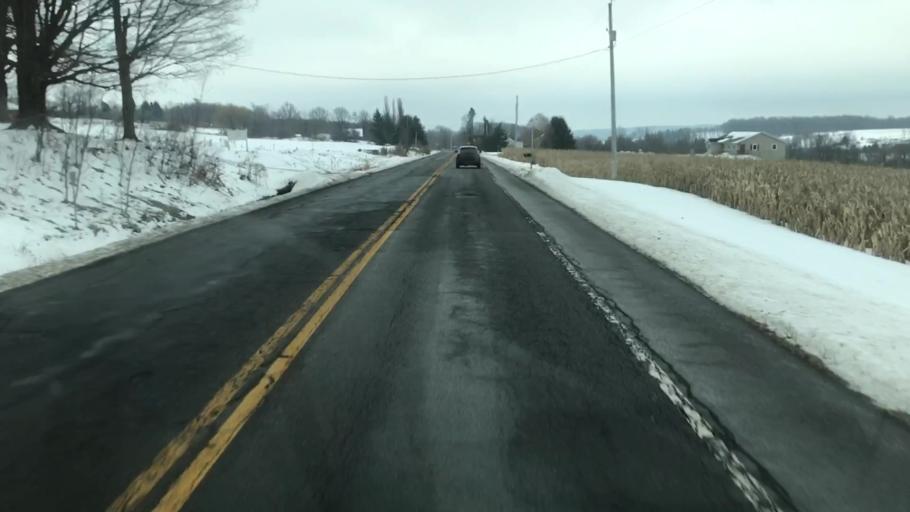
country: US
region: New York
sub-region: Cayuga County
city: Moravia
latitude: 42.7402
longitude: -76.3166
